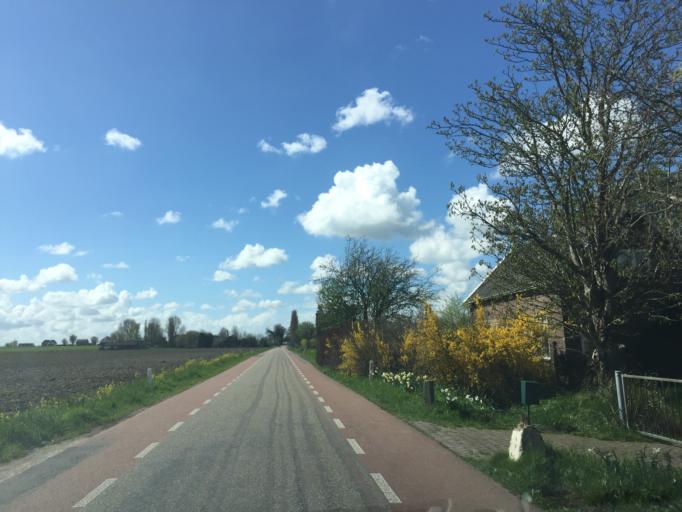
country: NL
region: South Holland
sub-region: Gemeente Kaag en Braassem
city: Leimuiden
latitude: 52.2106
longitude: 4.6772
